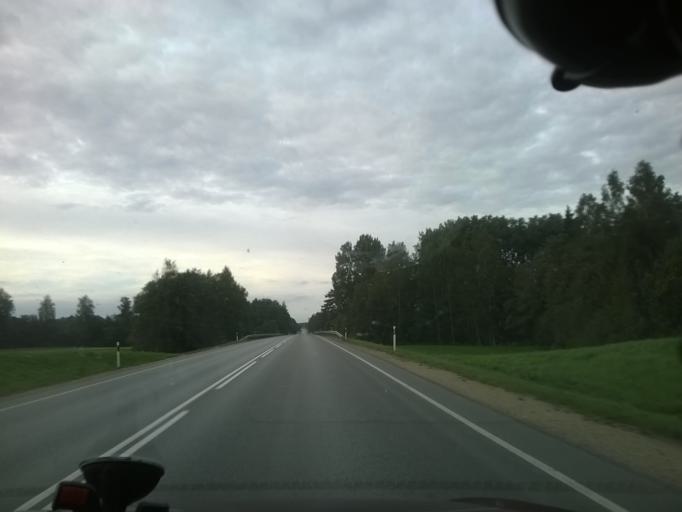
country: EE
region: Vorumaa
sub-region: Voru linn
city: Voru
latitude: 57.8941
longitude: 26.8462
